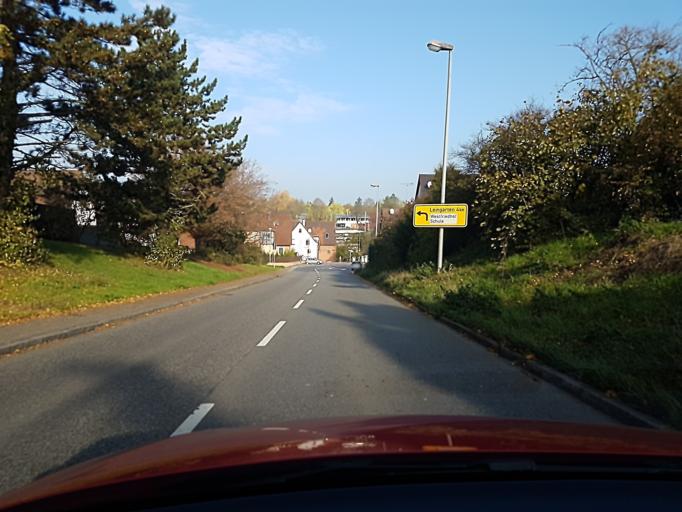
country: DE
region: Baden-Wuerttemberg
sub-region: Regierungsbezirk Stuttgart
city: Nordheim
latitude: 49.1184
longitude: 9.1536
